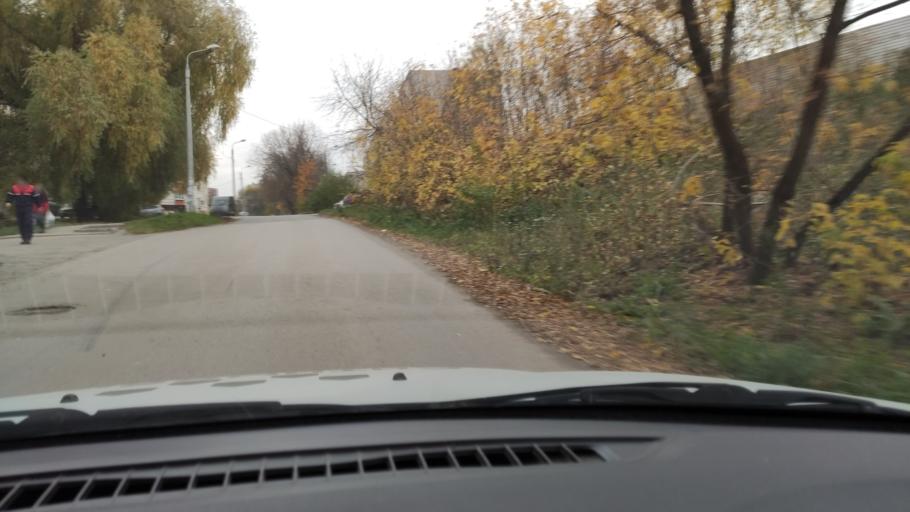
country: RU
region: Perm
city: Perm
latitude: 57.9902
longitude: 56.2389
